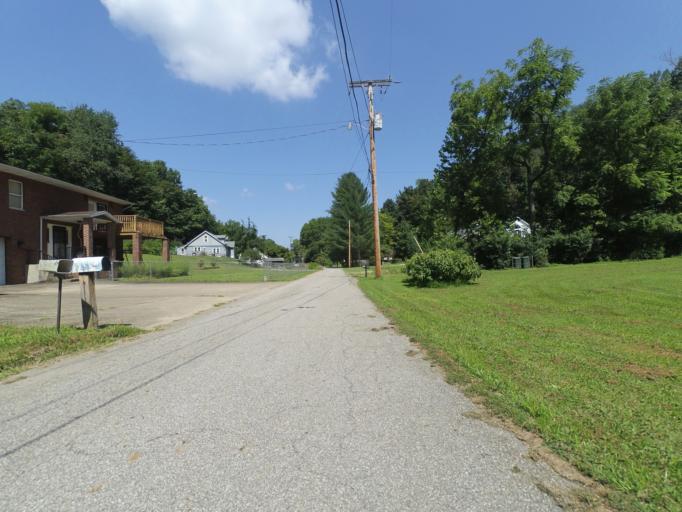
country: US
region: West Virginia
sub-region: Cabell County
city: Huntington
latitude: 38.3867
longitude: -82.4490
